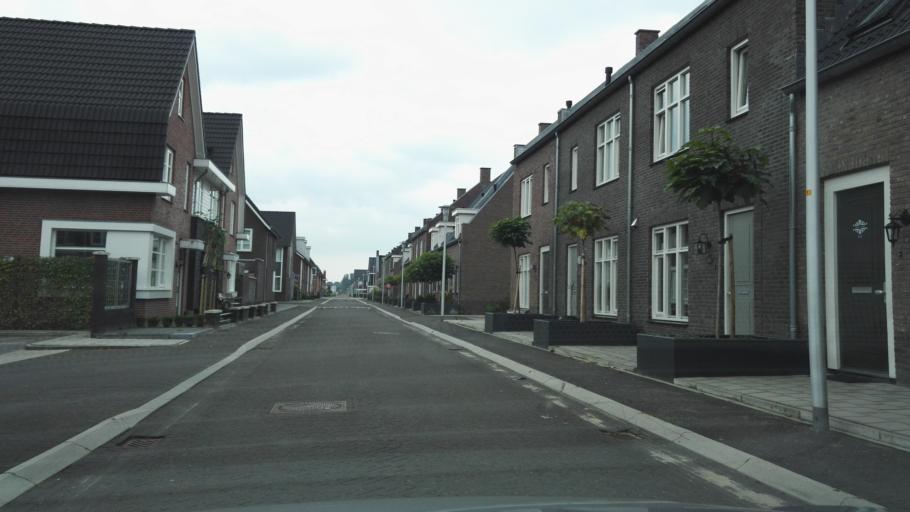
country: NL
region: Gelderland
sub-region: Gemeente Apeldoorn
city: Apeldoorn
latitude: 52.2406
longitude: 6.0004
